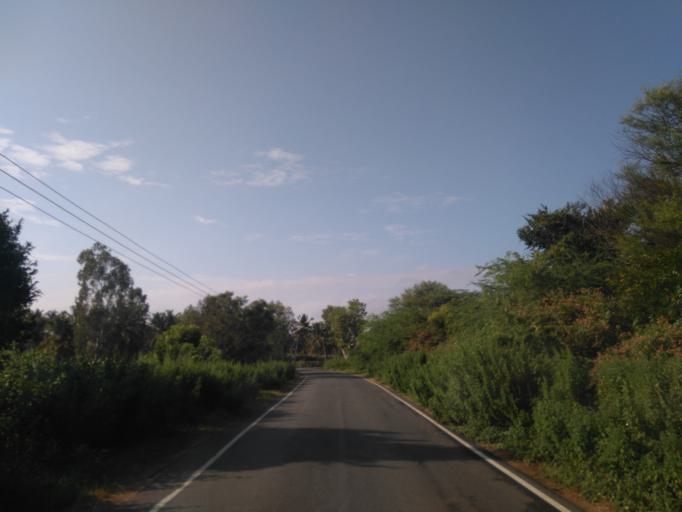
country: IN
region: Karnataka
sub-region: Mandya
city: Malavalli
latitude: 12.2971
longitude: 77.0712
